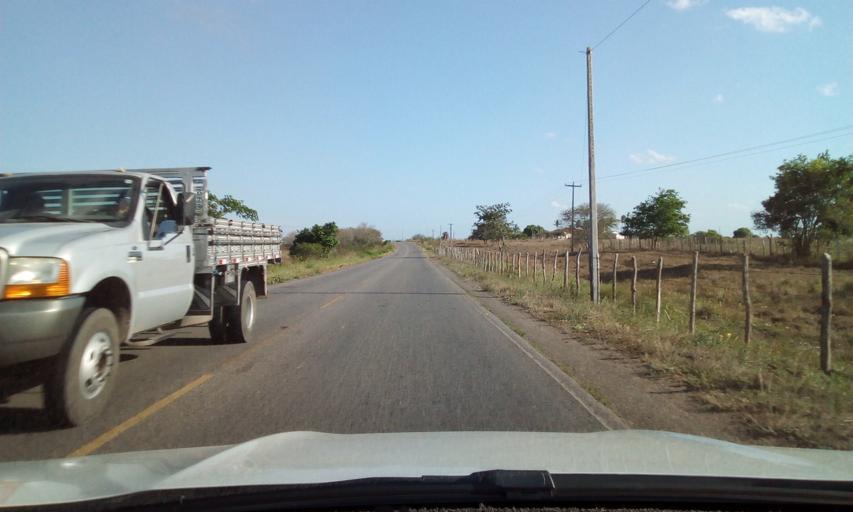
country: BR
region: Paraiba
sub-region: Guarabira
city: Guarabira
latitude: -6.9197
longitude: -35.4474
